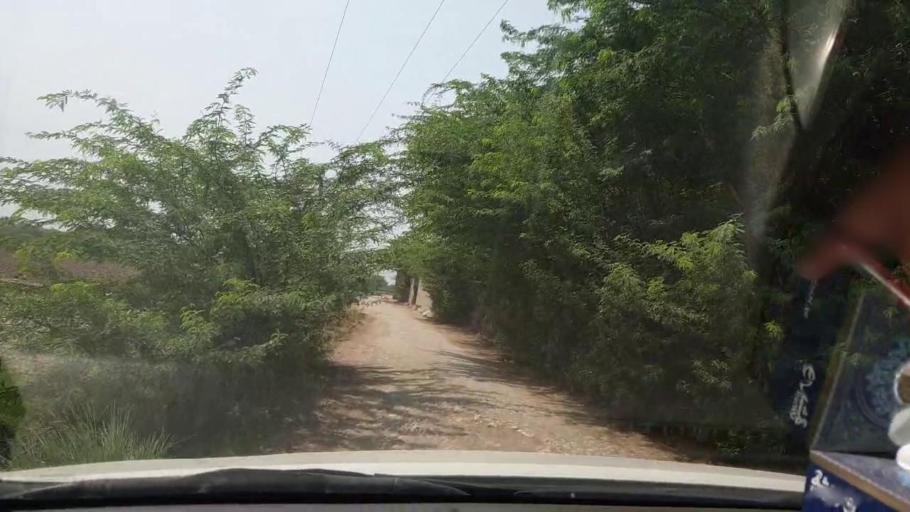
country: PK
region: Sindh
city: Shikarpur
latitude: 27.9917
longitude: 68.7125
